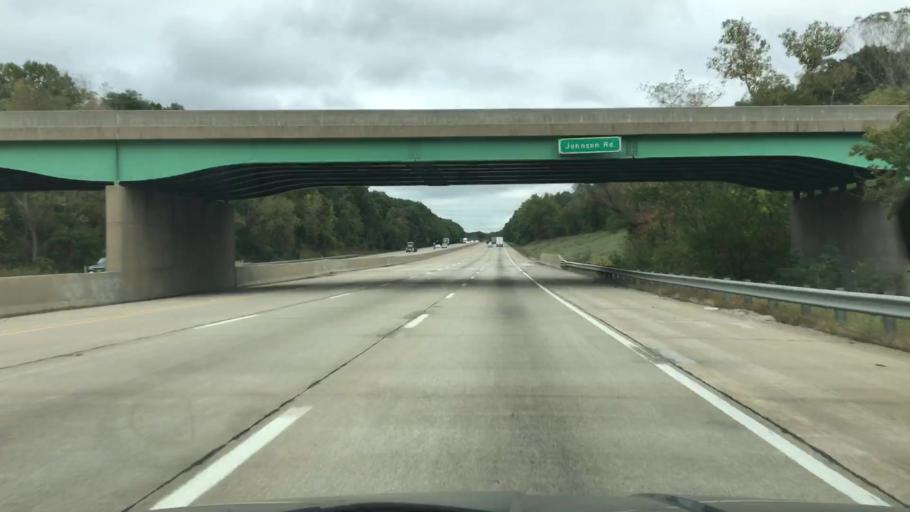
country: US
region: Indiana
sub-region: LaPorte County
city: Trail Creek
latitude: 41.6745
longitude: -86.8460
